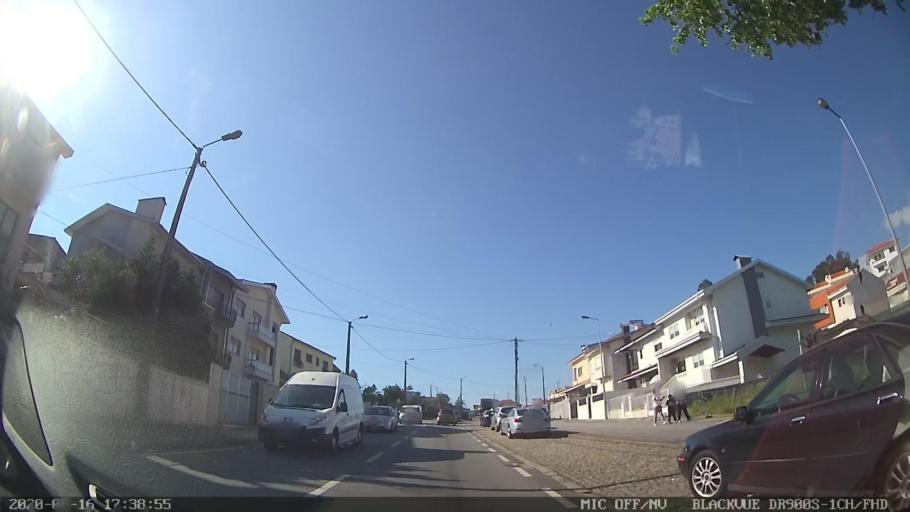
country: PT
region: Porto
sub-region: Valongo
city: Valongo
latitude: 41.1881
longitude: -8.5250
